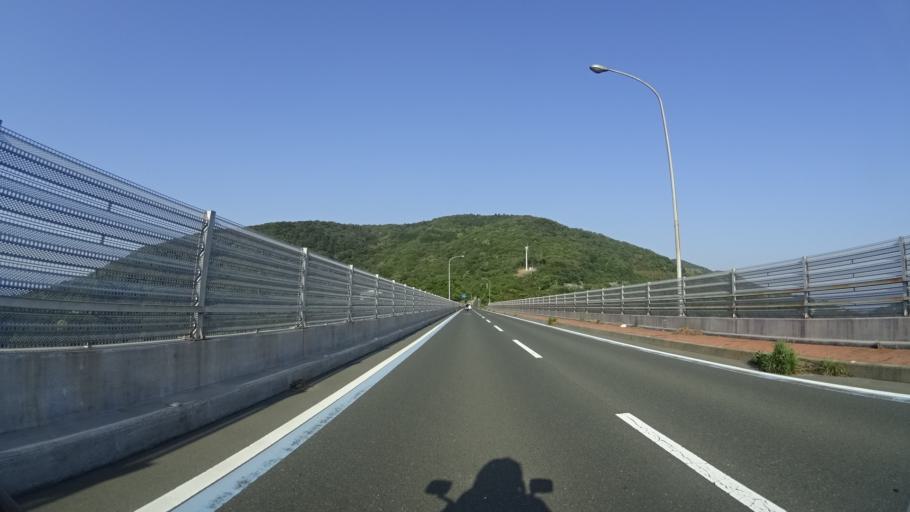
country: JP
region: Ehime
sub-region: Nishiuwa-gun
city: Ikata-cho
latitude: 33.4477
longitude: 132.2553
